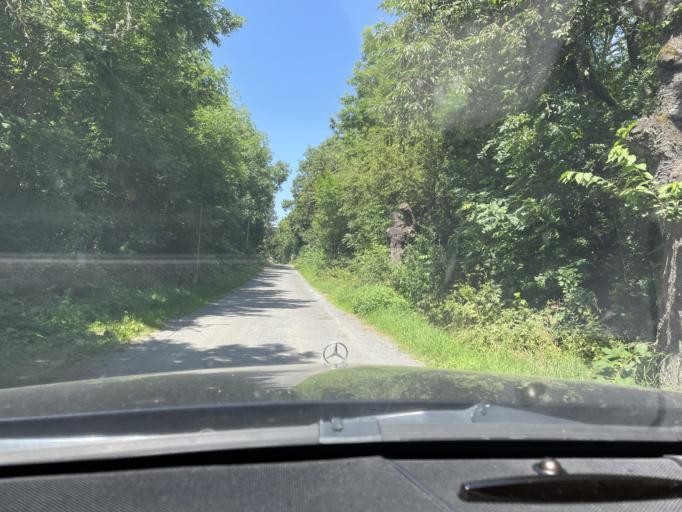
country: DE
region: Thuringia
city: Muehlhausen
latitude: 51.2106
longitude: 10.4255
